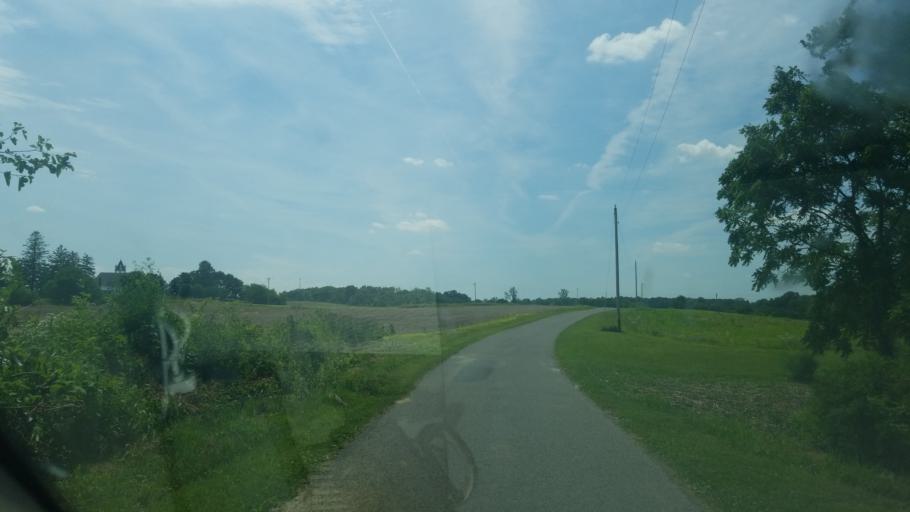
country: US
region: Ohio
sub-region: Hardin County
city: Ada
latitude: 40.6260
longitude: -83.8391
